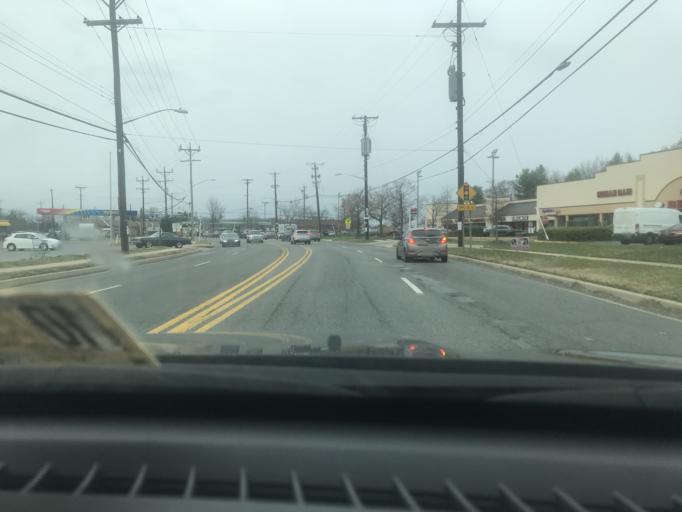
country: US
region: Maryland
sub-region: Prince George's County
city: Camp Springs
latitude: 38.7936
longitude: -76.9266
